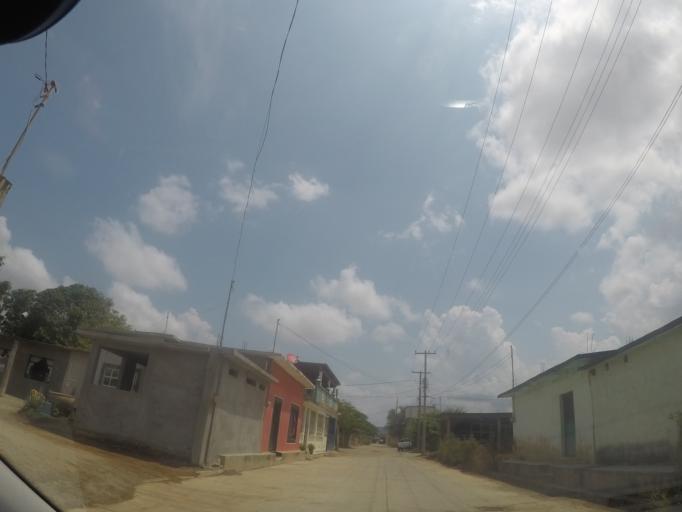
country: MX
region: Oaxaca
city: El Espinal
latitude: 16.5569
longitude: -94.9476
